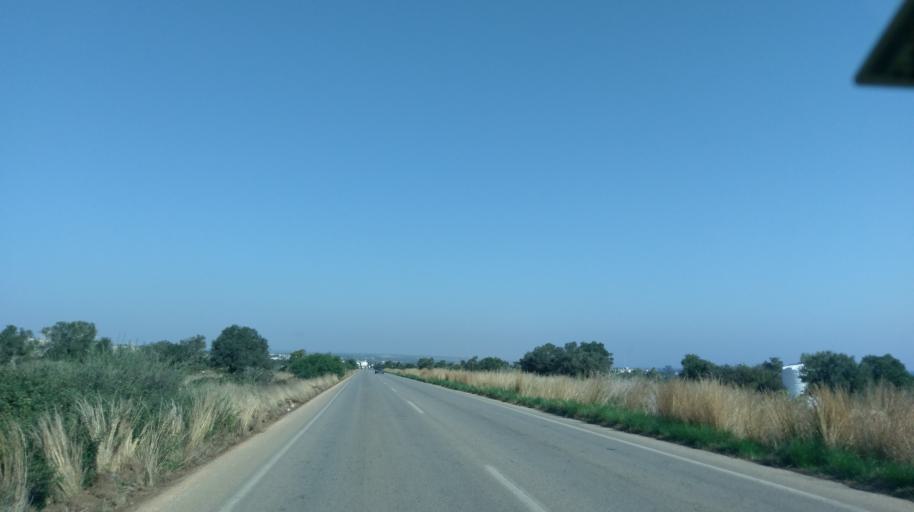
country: CY
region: Ammochostos
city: Leonarisso
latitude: 35.4114
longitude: 34.1143
